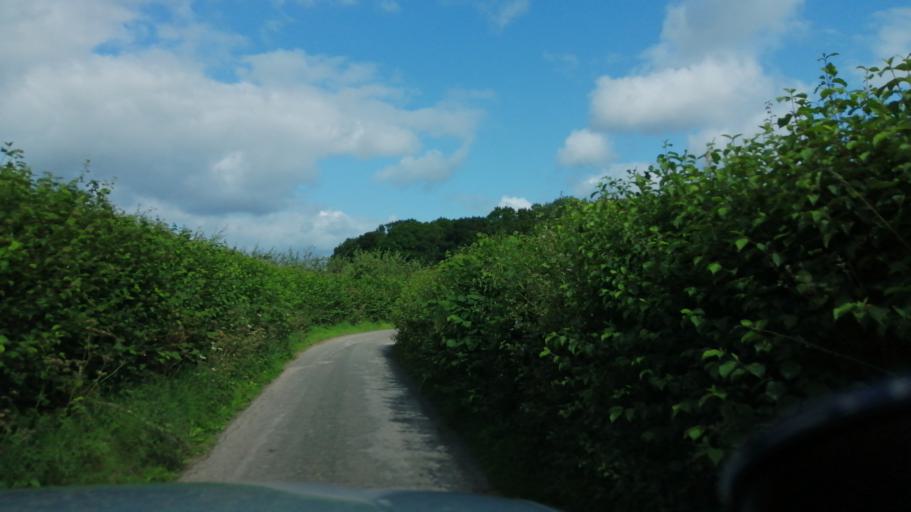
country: GB
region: England
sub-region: Herefordshire
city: Kinnersley
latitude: 52.1336
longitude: -2.9469
